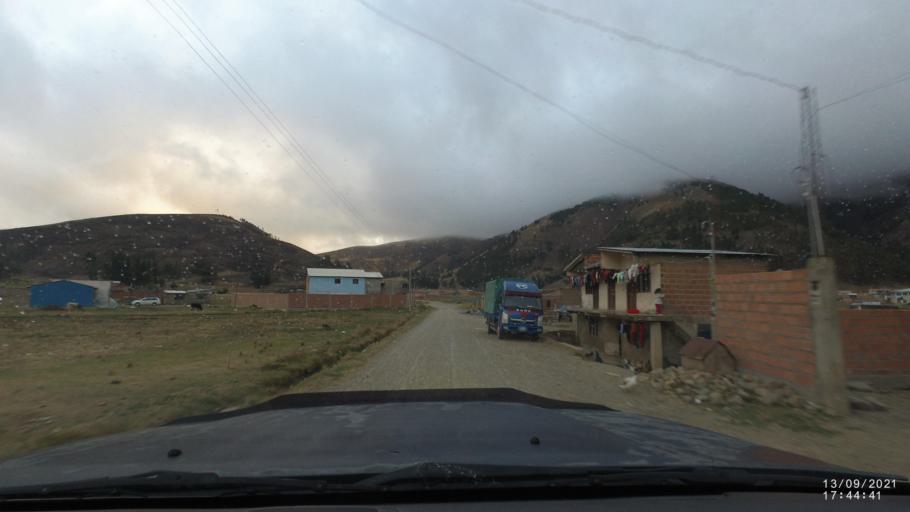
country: BO
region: Cochabamba
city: Colomi
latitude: -17.3732
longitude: -65.8302
